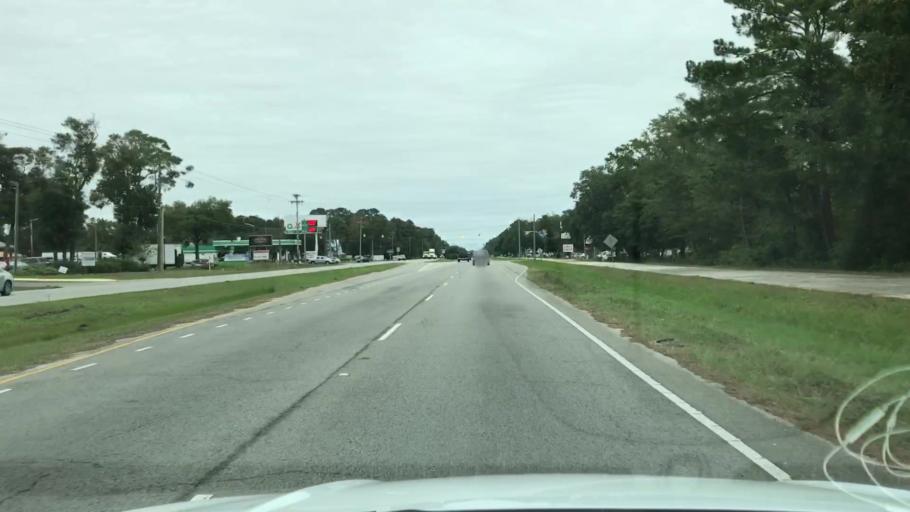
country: US
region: South Carolina
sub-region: Georgetown County
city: Murrells Inlet
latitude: 33.5346
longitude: -79.0585
